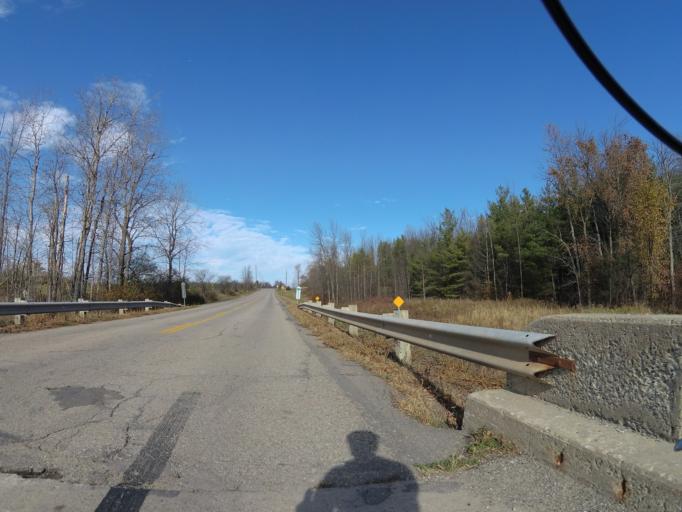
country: CA
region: Ontario
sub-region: Lanark County
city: Smiths Falls
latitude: 44.8328
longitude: -75.9352
